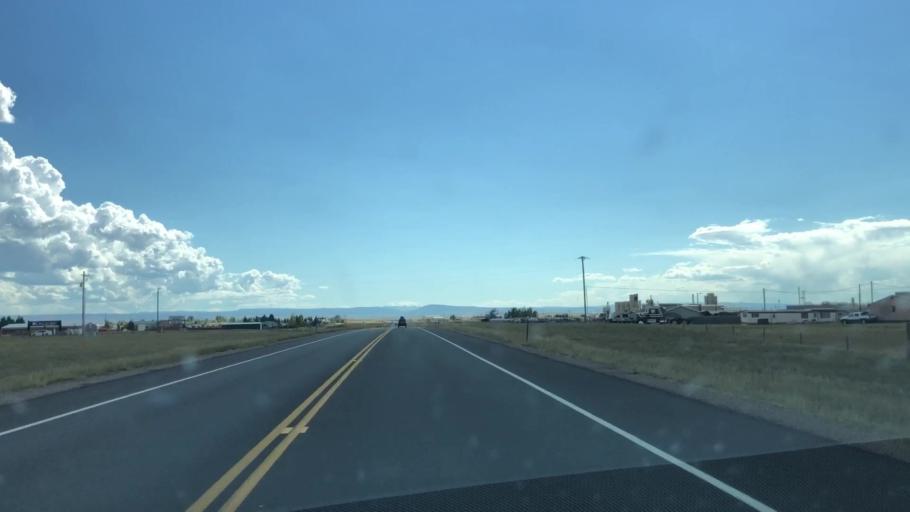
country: US
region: Wyoming
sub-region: Albany County
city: Laramie
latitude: 41.2722
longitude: -105.5940
